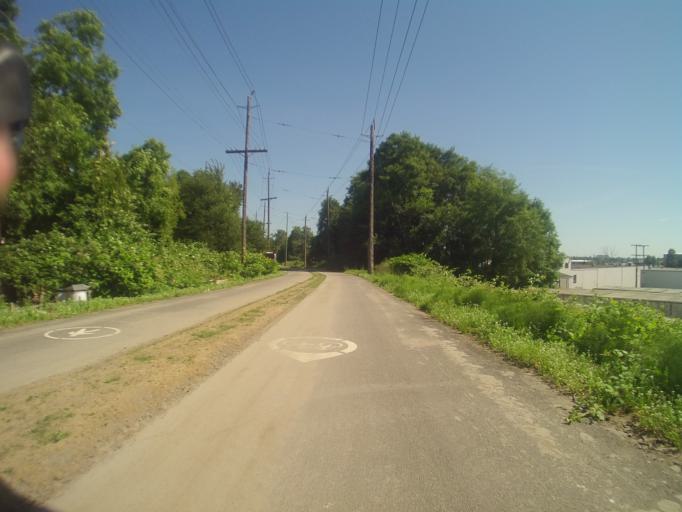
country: CA
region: British Columbia
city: Richmond
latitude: 49.2070
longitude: -123.1437
